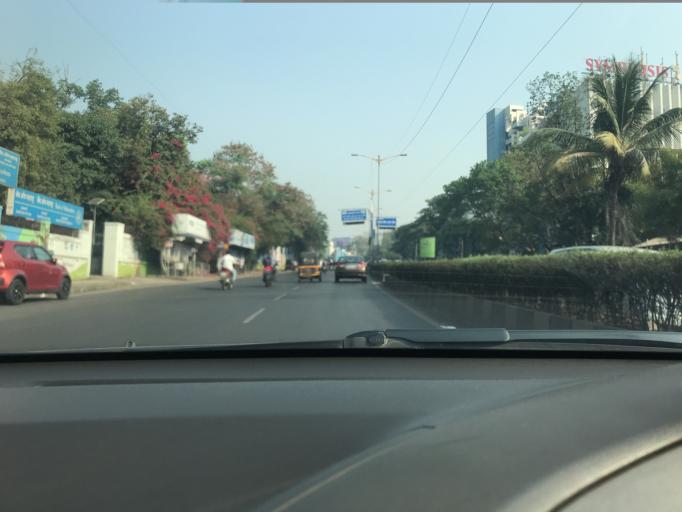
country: IN
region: Maharashtra
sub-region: Pune Division
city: Shivaji Nagar
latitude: 18.5214
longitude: 73.8291
